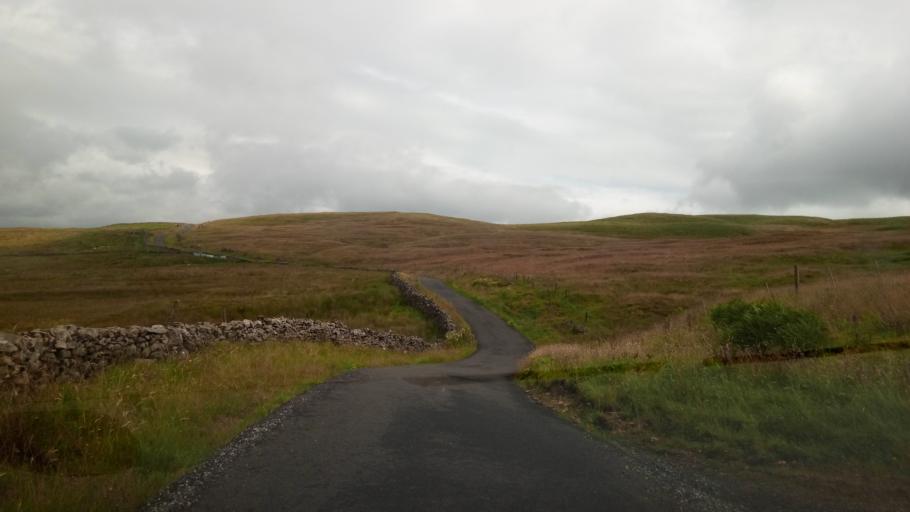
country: GB
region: England
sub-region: Cumbria
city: Kirkby Stephen
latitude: 54.2877
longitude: -2.3401
